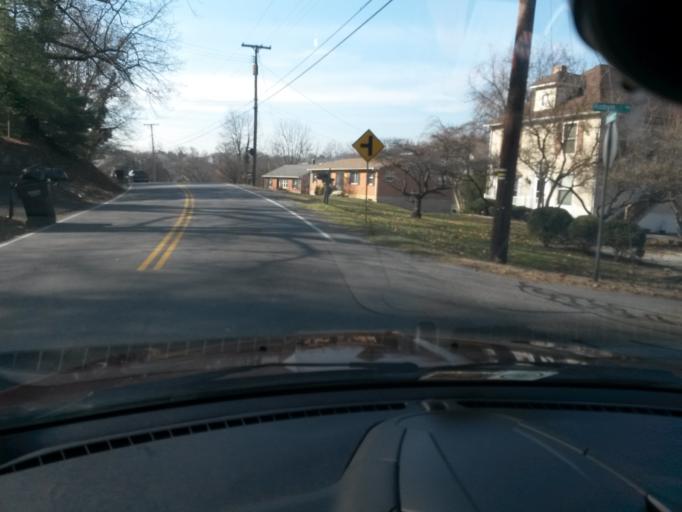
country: US
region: Virginia
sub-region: Roanoke County
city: Cave Spring
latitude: 37.2400
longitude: -79.9859
